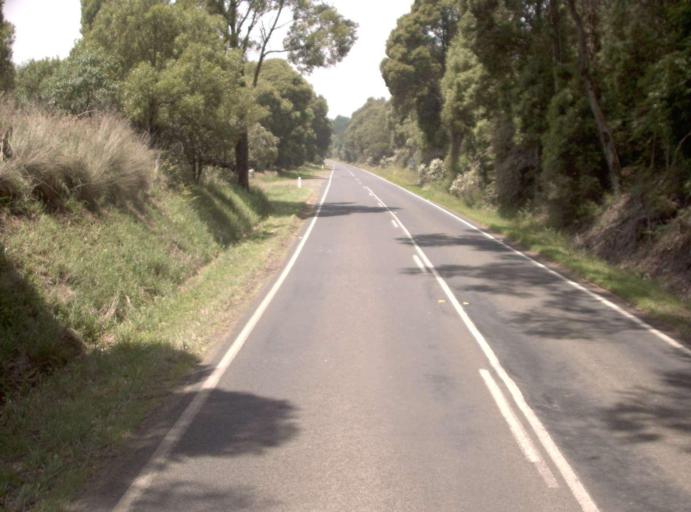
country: AU
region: Victoria
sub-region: Latrobe
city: Traralgon
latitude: -38.3538
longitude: 146.7159
